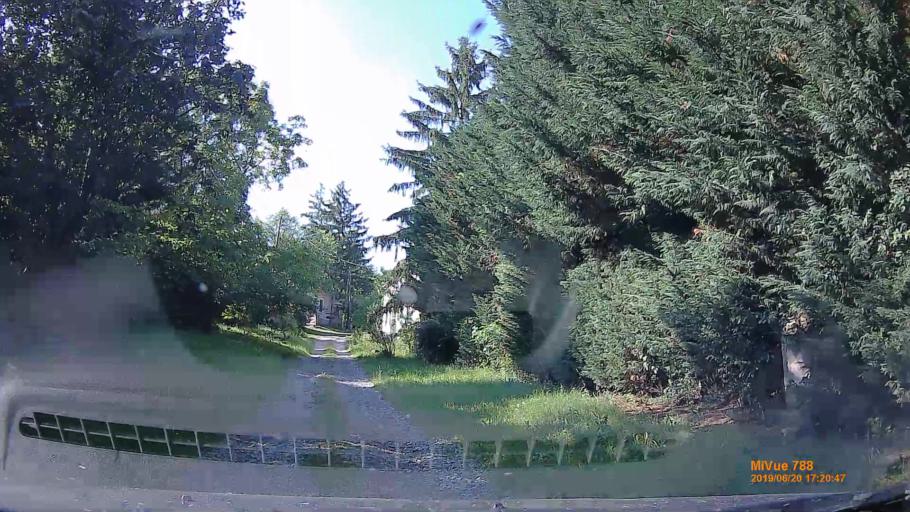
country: HU
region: Baranya
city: Buekkoesd
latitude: 46.1646
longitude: 18.0087
